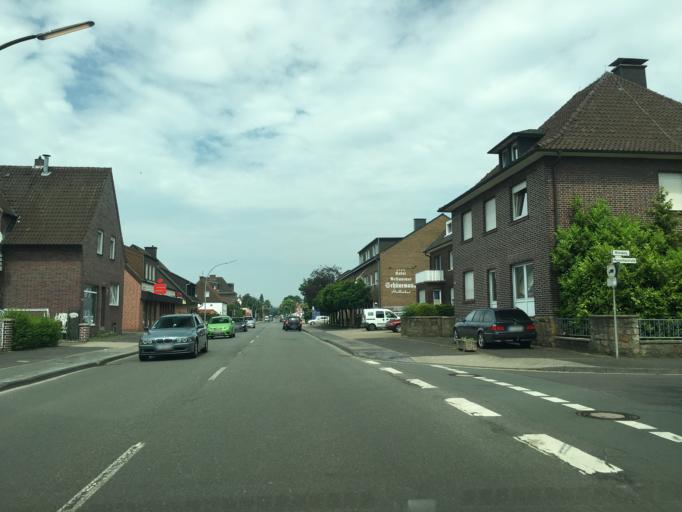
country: DE
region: North Rhine-Westphalia
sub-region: Regierungsbezirk Munster
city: Laer
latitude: 52.1118
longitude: 7.4006
